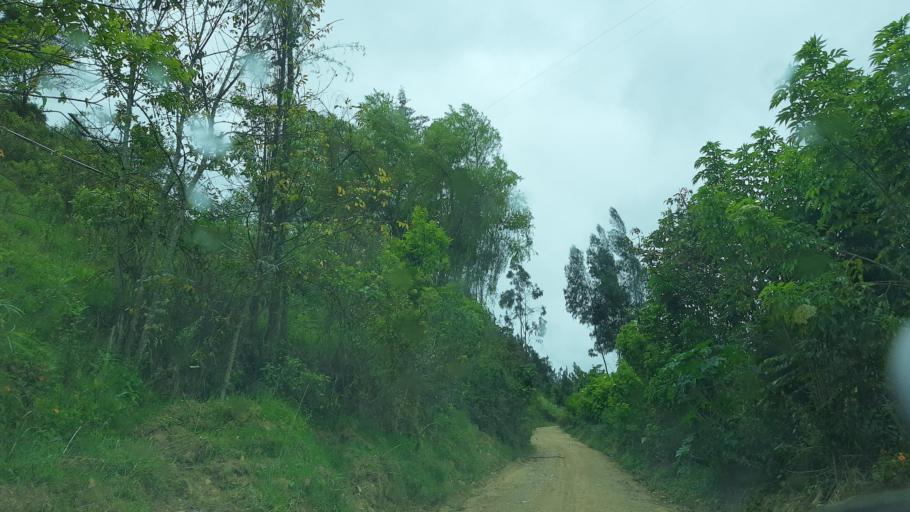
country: CO
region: Boyaca
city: Tibana
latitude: 5.3101
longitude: -73.4343
